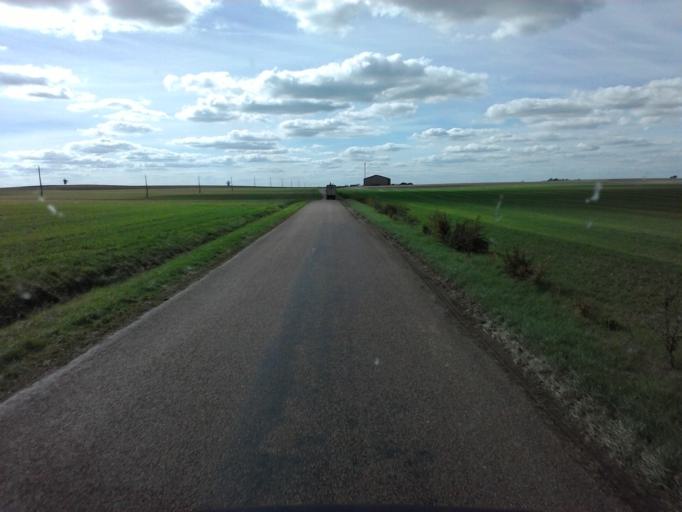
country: FR
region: Bourgogne
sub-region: Departement de la Cote-d'Or
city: Montbard
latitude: 47.7333
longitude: 4.4471
